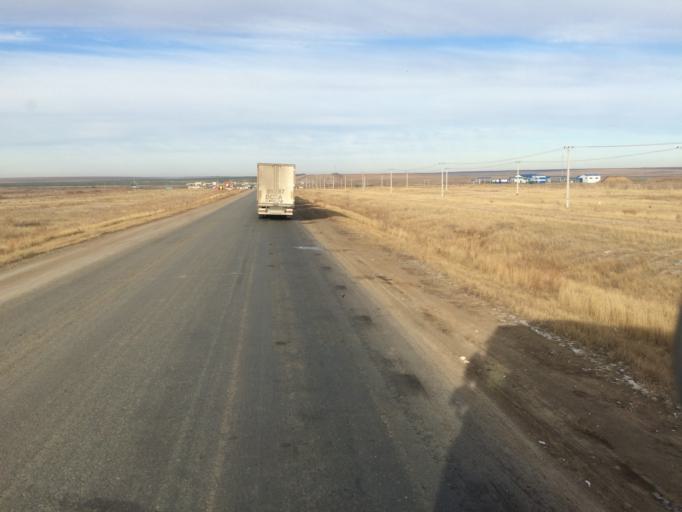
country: KZ
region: Batys Qazaqstan
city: Peremetnoe
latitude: 51.6598
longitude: 51.0085
